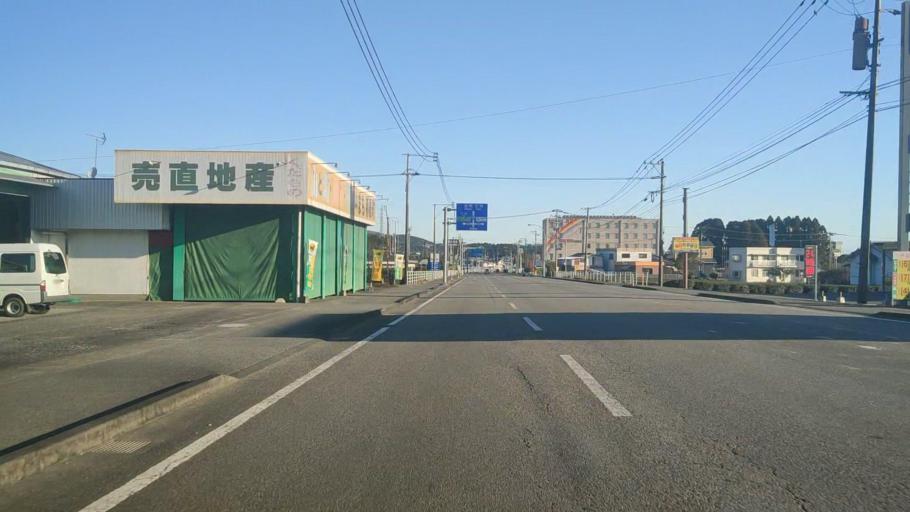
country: JP
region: Miyazaki
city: Takanabe
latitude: 32.2516
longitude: 131.5523
